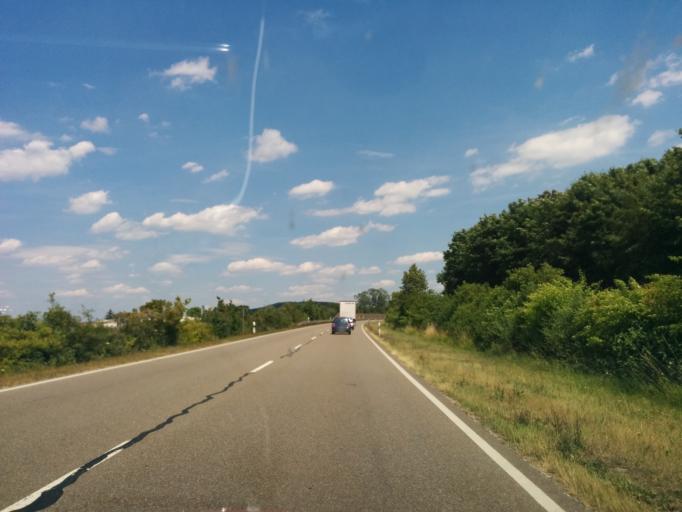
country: DE
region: Bavaria
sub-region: Regierungsbezirk Mittelfranken
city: Weissenburg in Bayern
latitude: 49.0195
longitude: 10.9664
